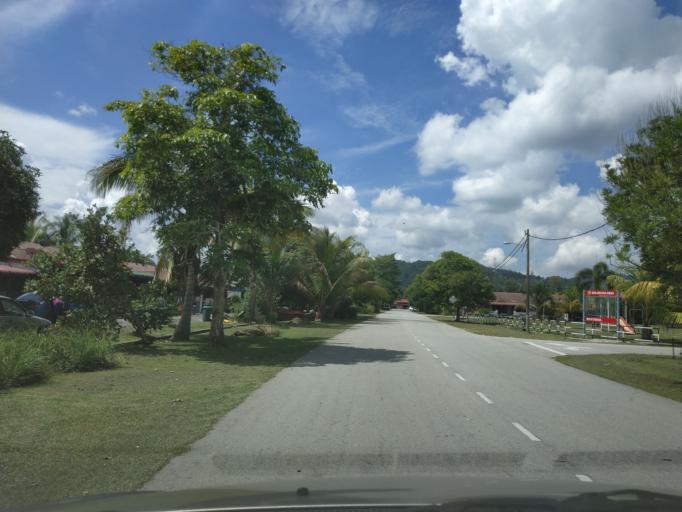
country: MY
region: Perak
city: Parit Buntar
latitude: 5.1384
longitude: 100.5958
